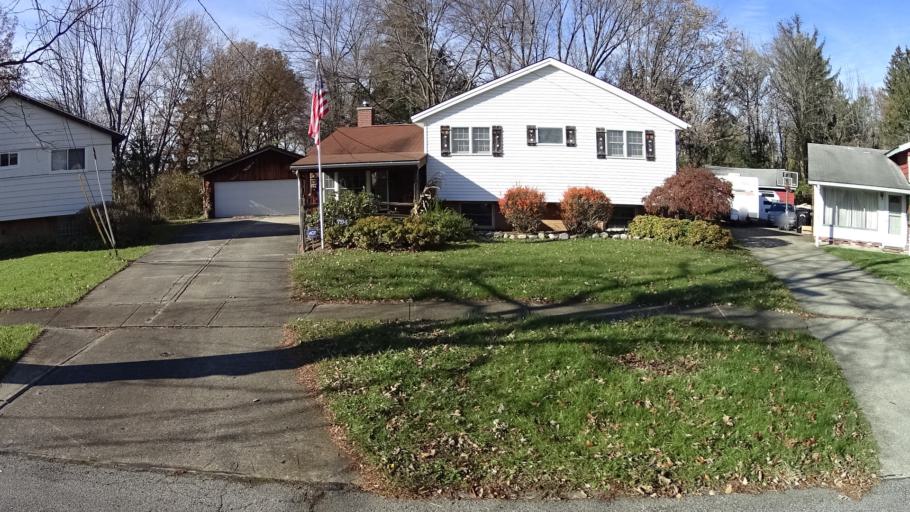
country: US
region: Ohio
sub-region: Lorain County
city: Sheffield
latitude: 41.4044
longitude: -82.0752
